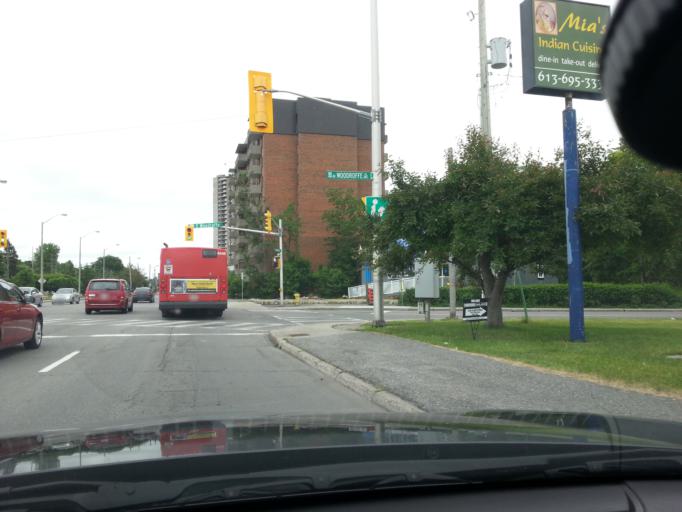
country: CA
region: Ontario
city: Bells Corners
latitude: 45.3779
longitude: -75.7747
